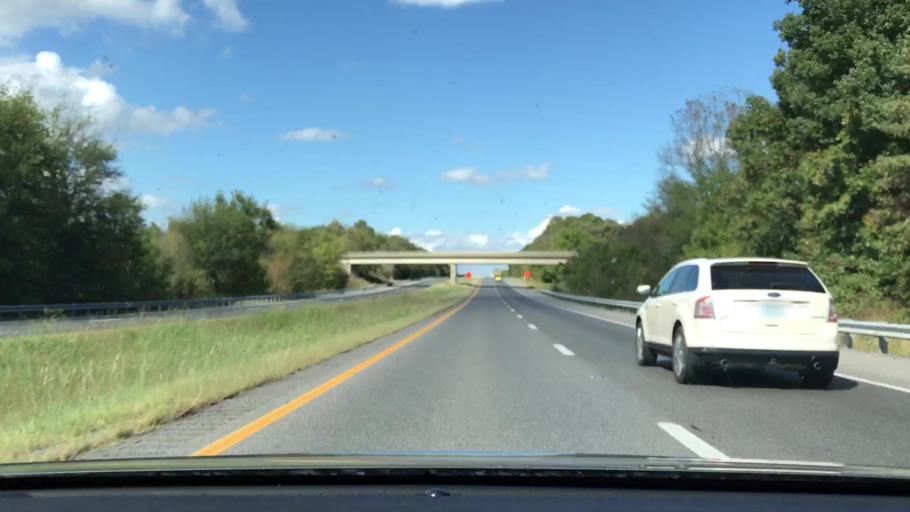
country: US
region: Kentucky
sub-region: Marshall County
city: Calvert City
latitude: 36.9541
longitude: -88.3498
